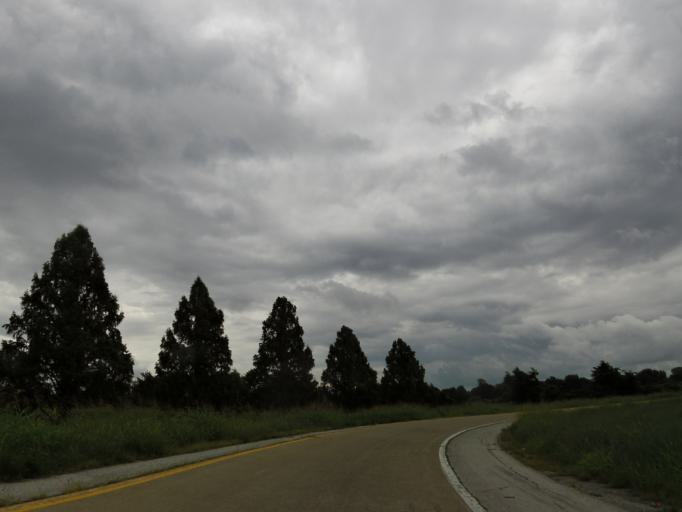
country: US
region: Illinois
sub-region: Alexander County
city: Cairo
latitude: 37.0448
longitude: -89.2002
